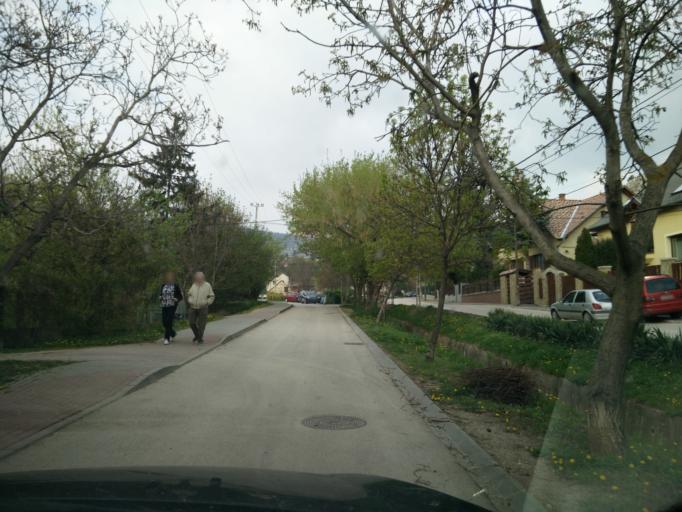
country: HU
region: Pest
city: Budaors
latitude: 47.4641
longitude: 18.9521
